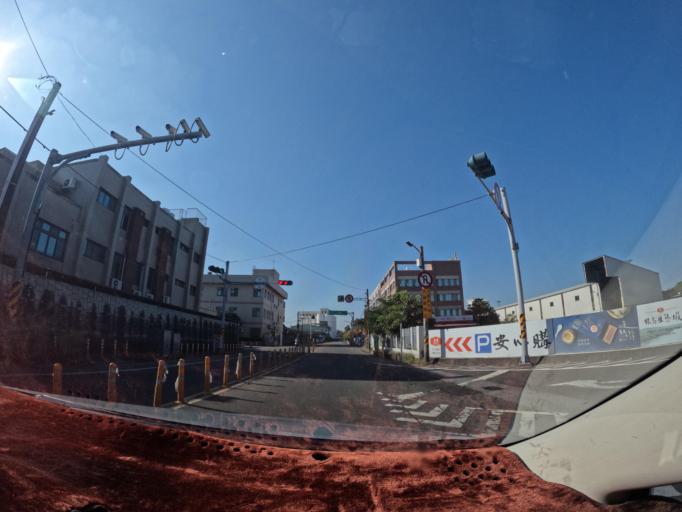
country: TW
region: Taiwan
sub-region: Tainan
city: Tainan
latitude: 23.0416
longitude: 120.2544
